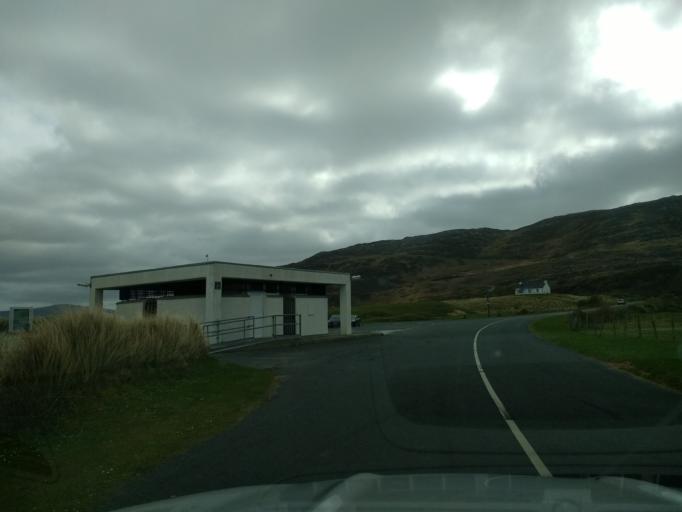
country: IE
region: Ulster
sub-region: County Donegal
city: Ramelton
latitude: 55.1884
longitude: -7.6099
